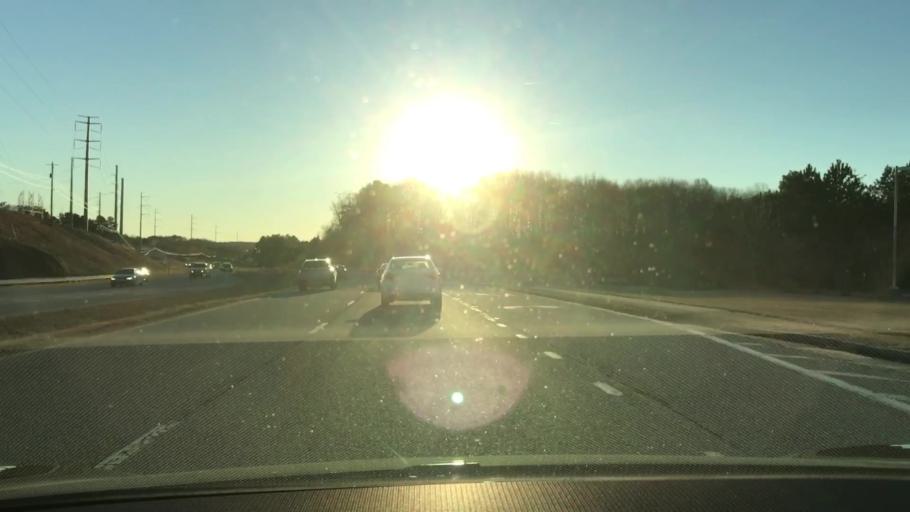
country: US
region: Georgia
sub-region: Gwinnett County
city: Buford
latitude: 34.1343
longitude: -84.0042
